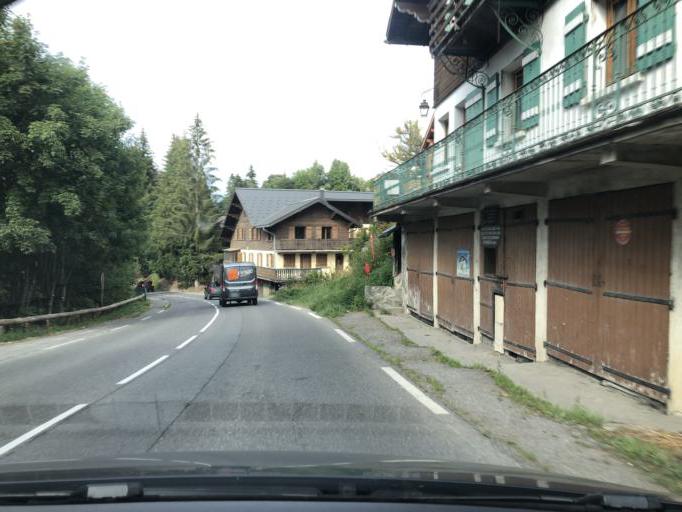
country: FR
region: Rhone-Alpes
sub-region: Departement de la Haute-Savoie
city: Megeve
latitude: 45.8609
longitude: 6.6304
